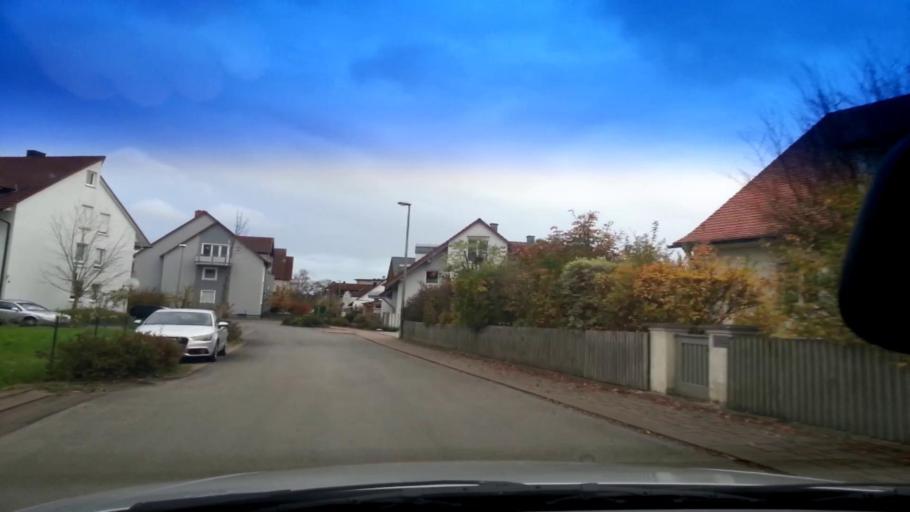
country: DE
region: Bavaria
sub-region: Upper Franconia
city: Gundelsheim
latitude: 49.9273
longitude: 10.9257
